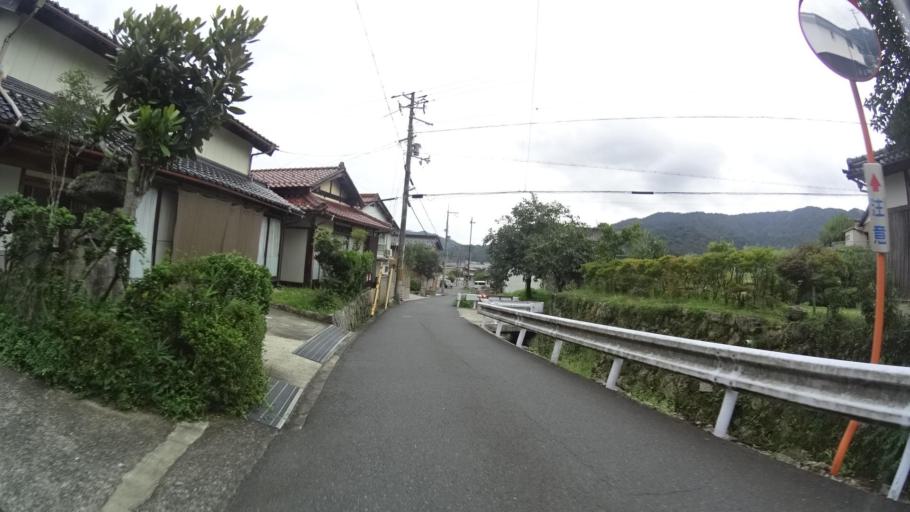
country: JP
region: Kyoto
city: Miyazu
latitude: 35.5276
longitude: 135.1857
